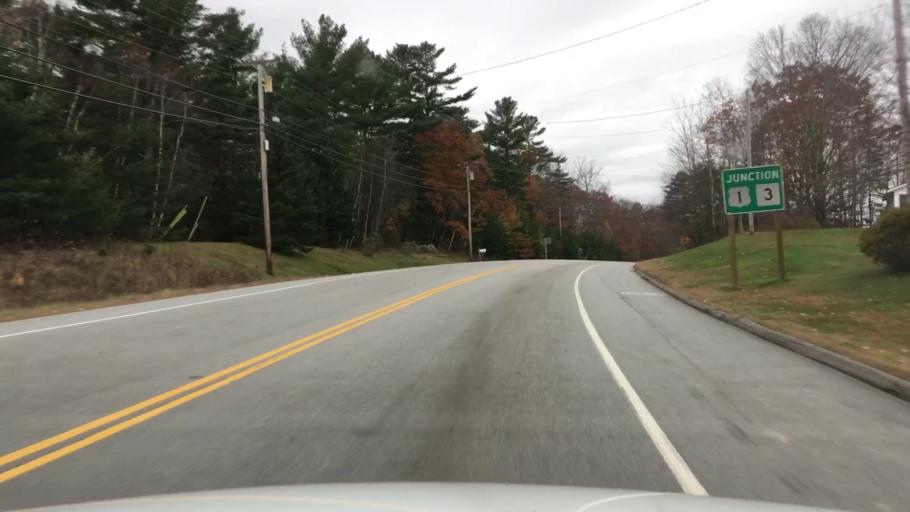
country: US
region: Maine
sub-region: Hancock County
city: Orland
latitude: 44.5588
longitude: -68.7067
